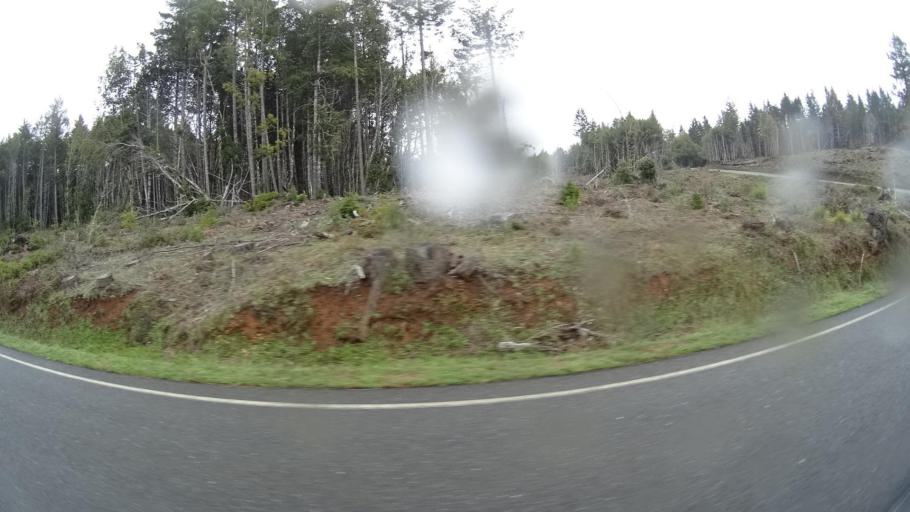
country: US
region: California
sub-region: Humboldt County
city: Willow Creek
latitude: 41.1638
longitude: -123.8188
